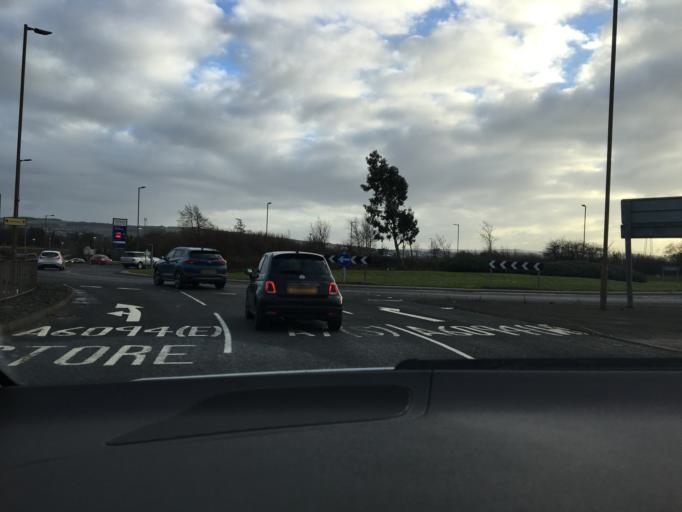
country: GB
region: Scotland
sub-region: Midlothian
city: Bonnyrigg
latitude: 55.8828
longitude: -3.0895
